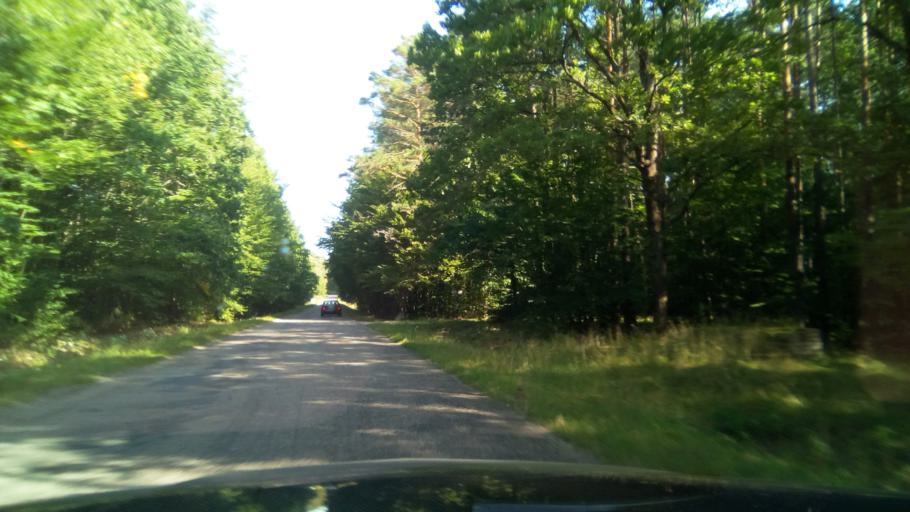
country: PL
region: Greater Poland Voivodeship
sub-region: Powiat zlotowski
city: Sypniewo
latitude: 53.4241
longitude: 16.5961
